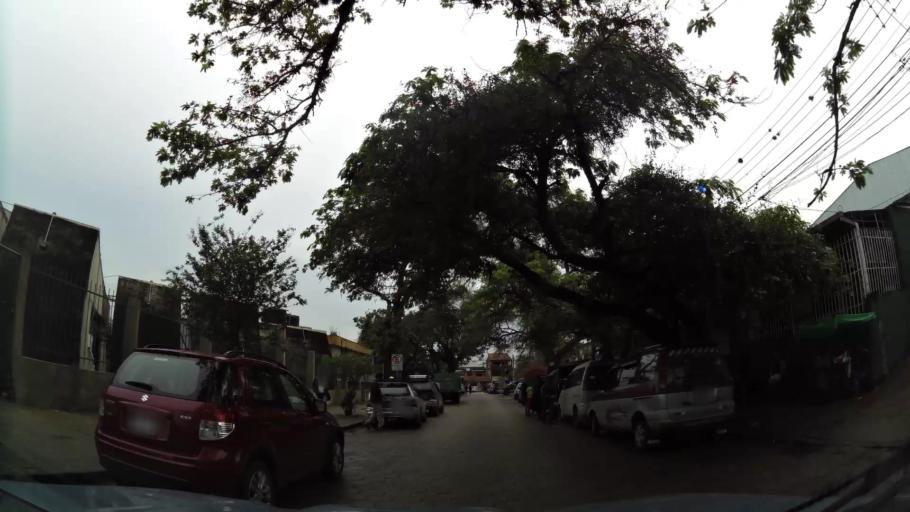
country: BO
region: Santa Cruz
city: Santa Cruz de la Sierra
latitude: -17.7925
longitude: -63.1859
